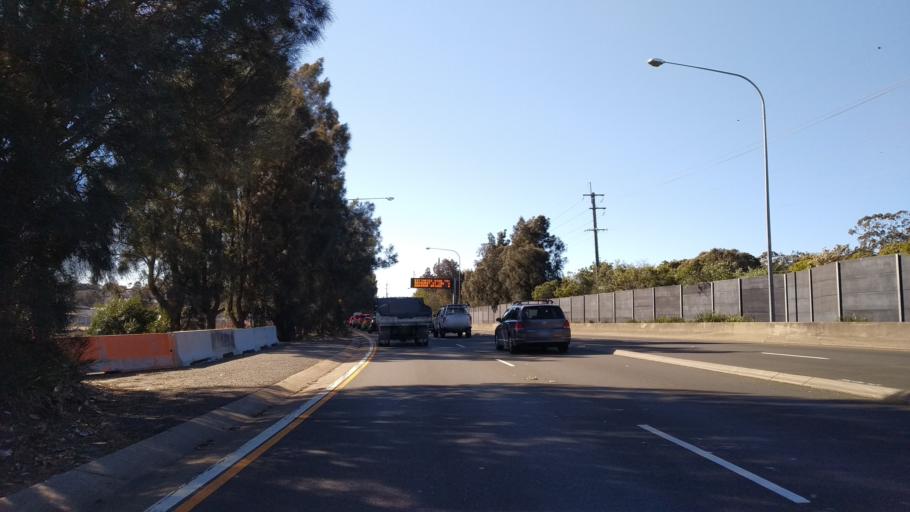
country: AU
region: New South Wales
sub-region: Leichhardt
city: Lilyfield
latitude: -33.8733
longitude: 151.1691
